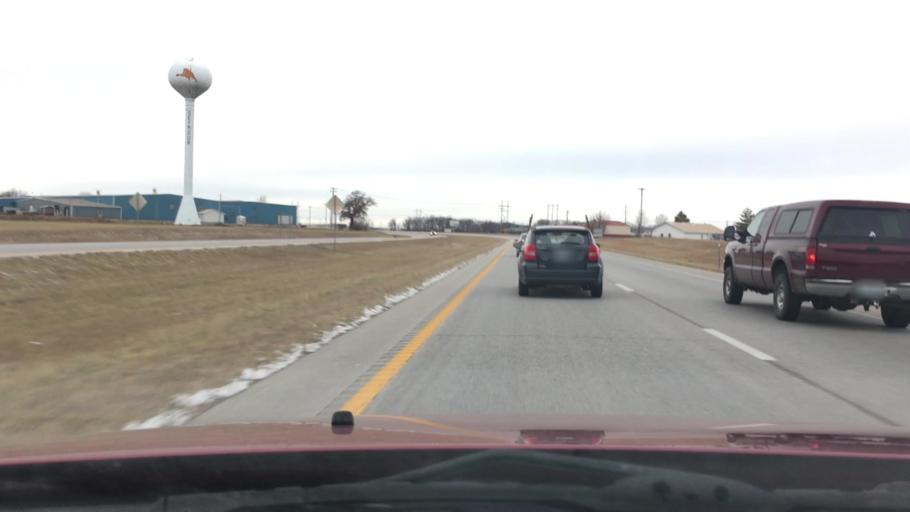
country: US
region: Missouri
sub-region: Webster County
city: Seymour
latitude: 37.1523
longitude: -92.7558
